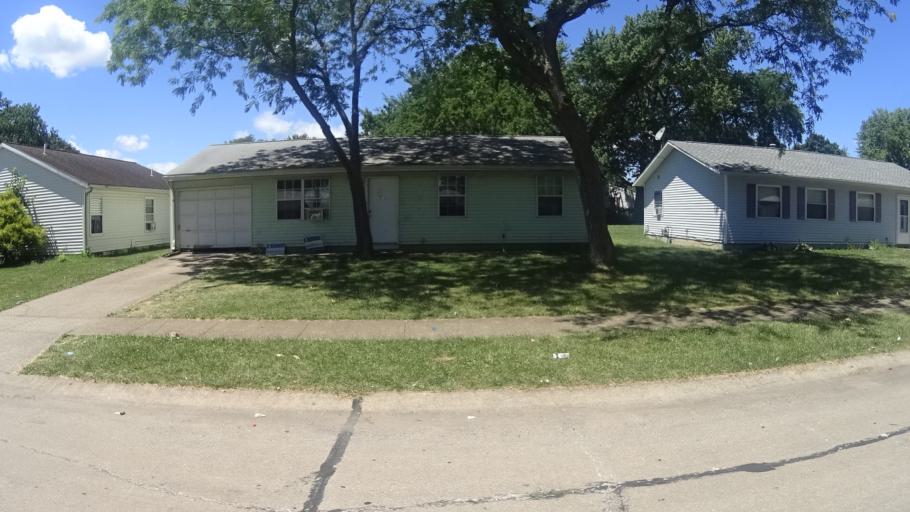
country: US
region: Ohio
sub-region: Erie County
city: Sandusky
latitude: 41.4393
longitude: -82.6863
